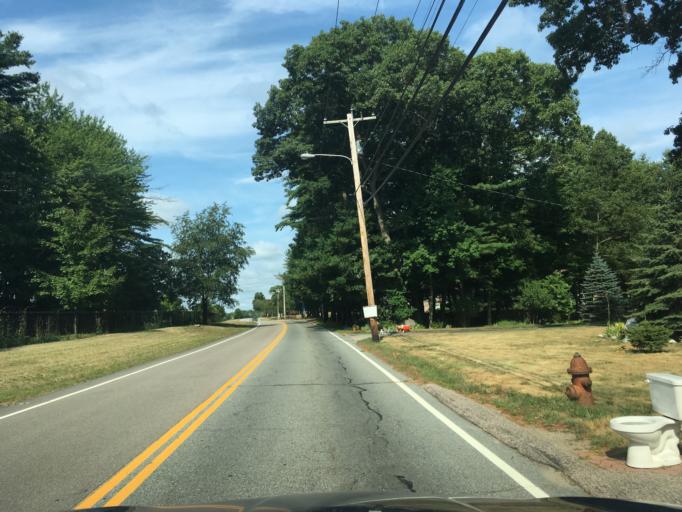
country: US
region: Rhode Island
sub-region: Kent County
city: East Greenwich
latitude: 41.6083
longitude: -71.4488
